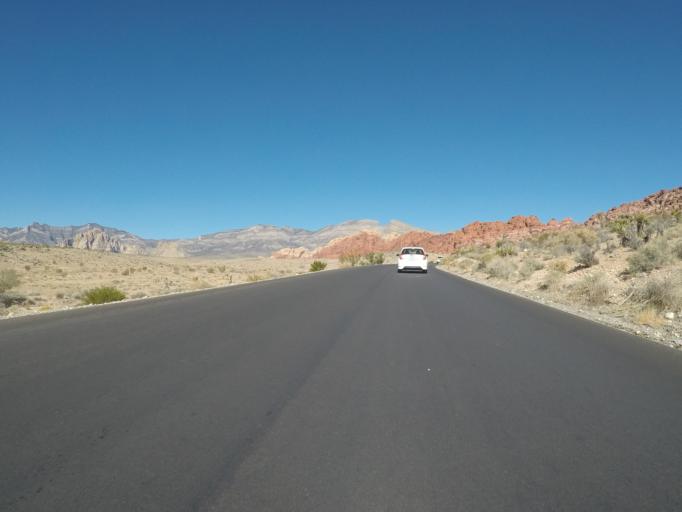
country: US
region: Nevada
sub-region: Clark County
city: Summerlin South
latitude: 36.1392
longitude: -115.4273
